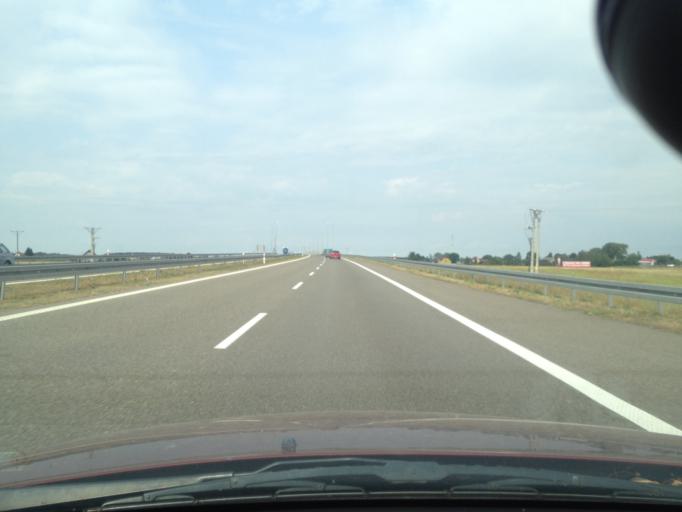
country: PL
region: West Pomeranian Voivodeship
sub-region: Powiat pyrzycki
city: Lipiany
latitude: 52.9464
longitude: 14.9649
